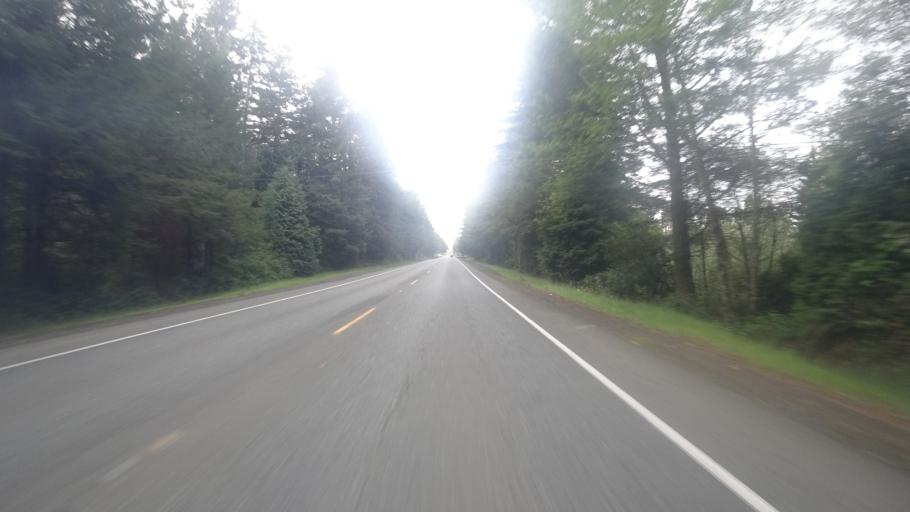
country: US
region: Oregon
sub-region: Coos County
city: Lakeside
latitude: 43.5314
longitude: -124.2157
